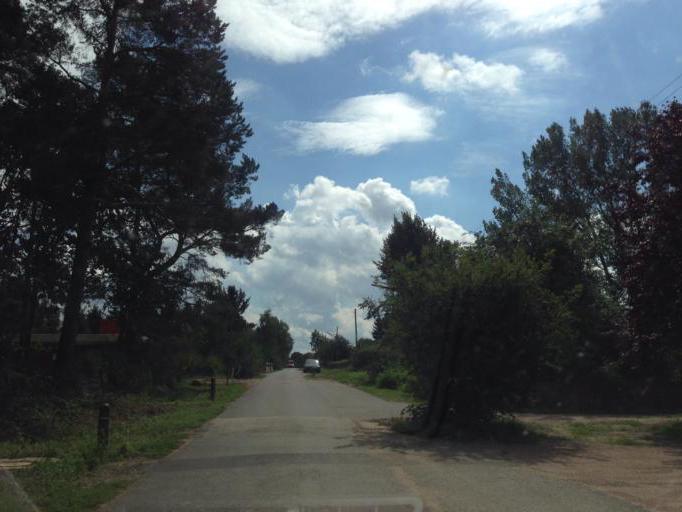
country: DE
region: Lower Saxony
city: Adendorf
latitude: 53.2944
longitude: 10.4408
